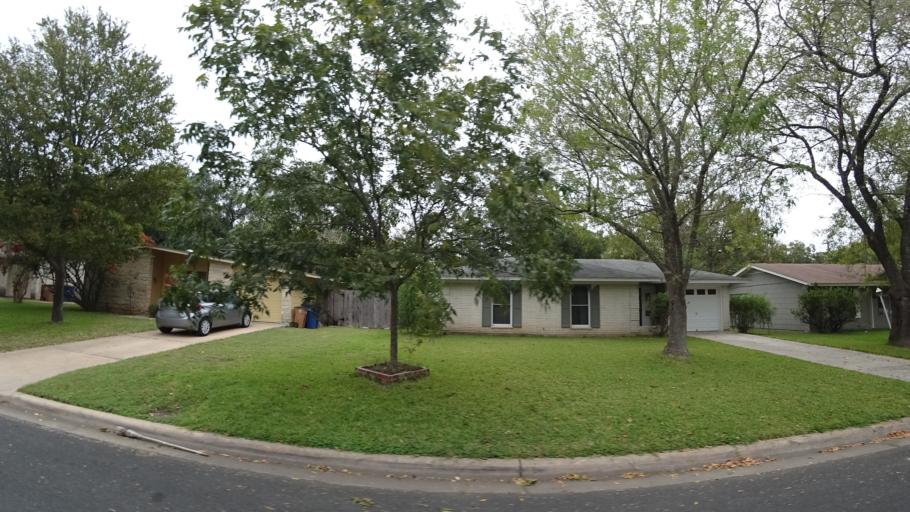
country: US
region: Texas
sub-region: Travis County
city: Austin
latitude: 30.2116
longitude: -97.7773
